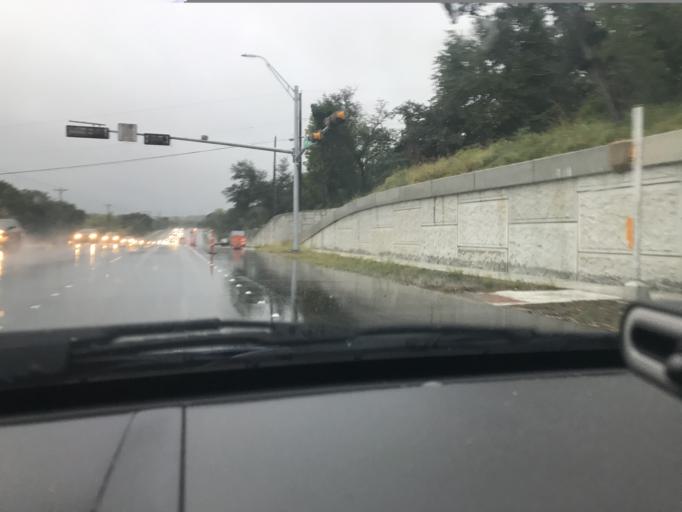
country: US
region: Texas
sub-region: Travis County
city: West Lake Hills
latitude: 30.2876
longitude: -97.8149
